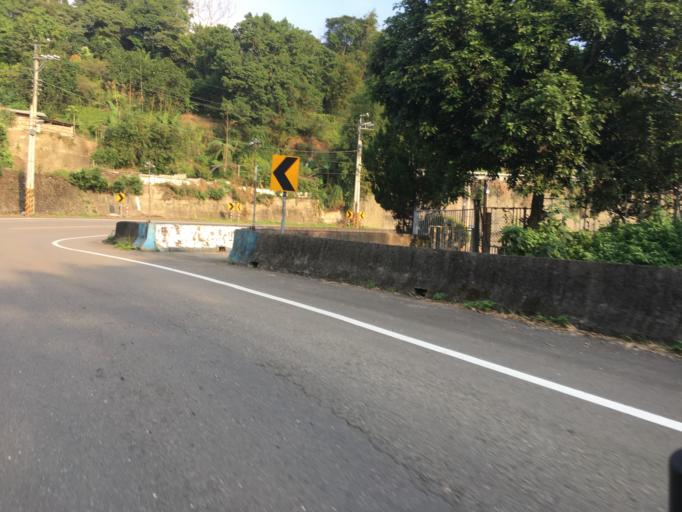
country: TW
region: Taiwan
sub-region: Hsinchu
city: Hsinchu
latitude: 24.7080
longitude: 121.0449
